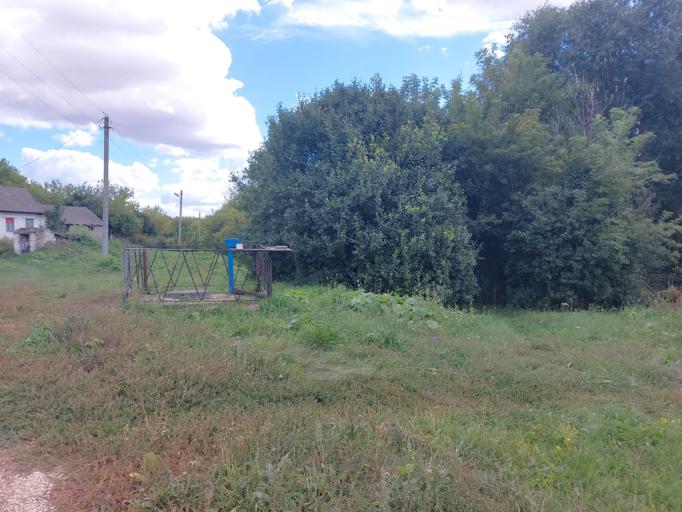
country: RU
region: Lipetsk
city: Terbuny
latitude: 52.2590
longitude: 38.2090
